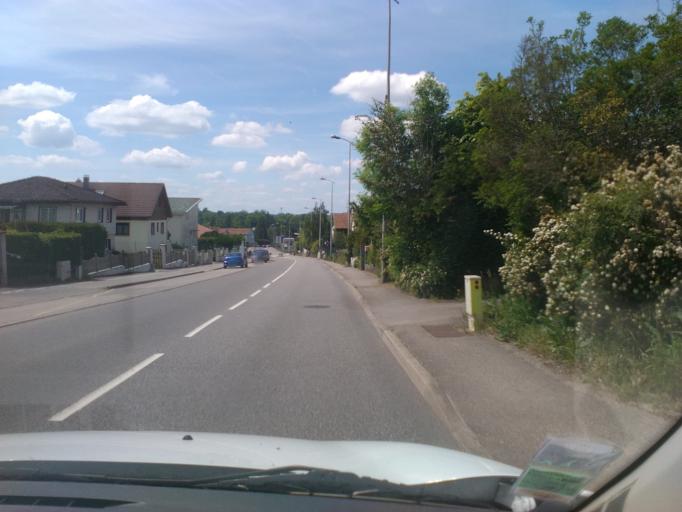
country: FR
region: Lorraine
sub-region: Departement des Vosges
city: Epinal
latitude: 48.1770
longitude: 6.4746
